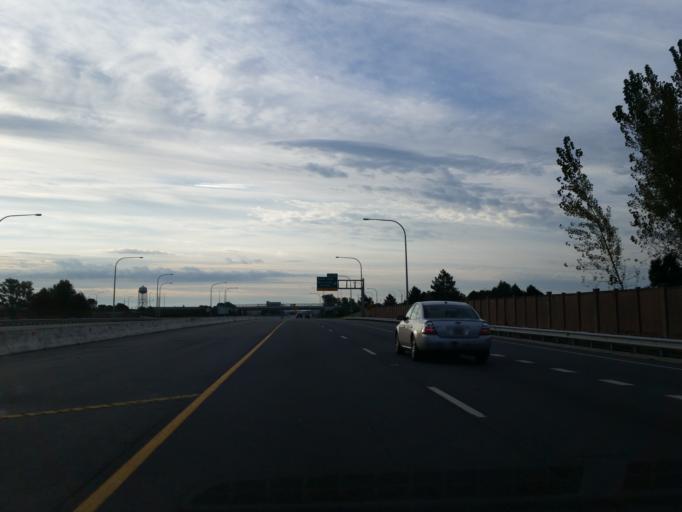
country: US
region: Delaware
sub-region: Kent County
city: Dover Base Housing
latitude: 39.1240
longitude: -75.4848
